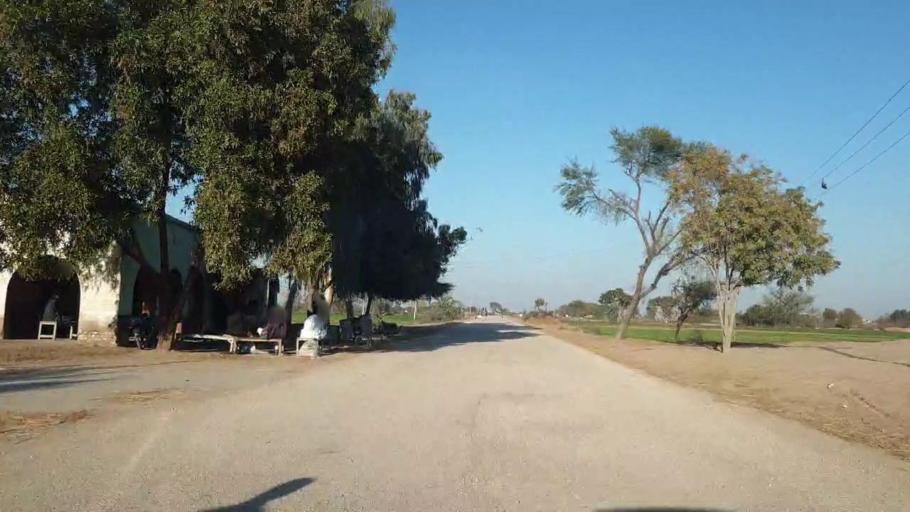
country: PK
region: Sindh
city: Dokri
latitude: 27.3691
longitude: 68.1171
